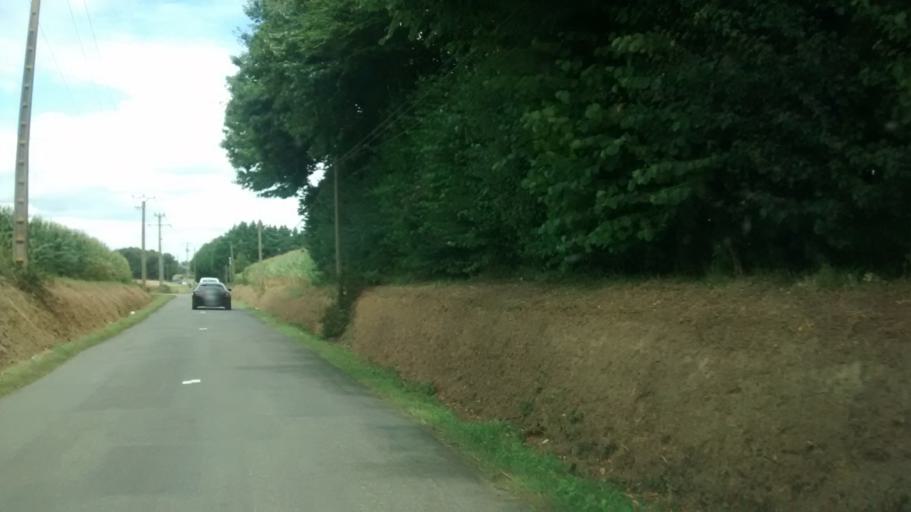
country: FR
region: Brittany
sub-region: Departement d'Ille-et-Vilaine
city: Tinteniac
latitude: 48.3014
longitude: -1.8469
